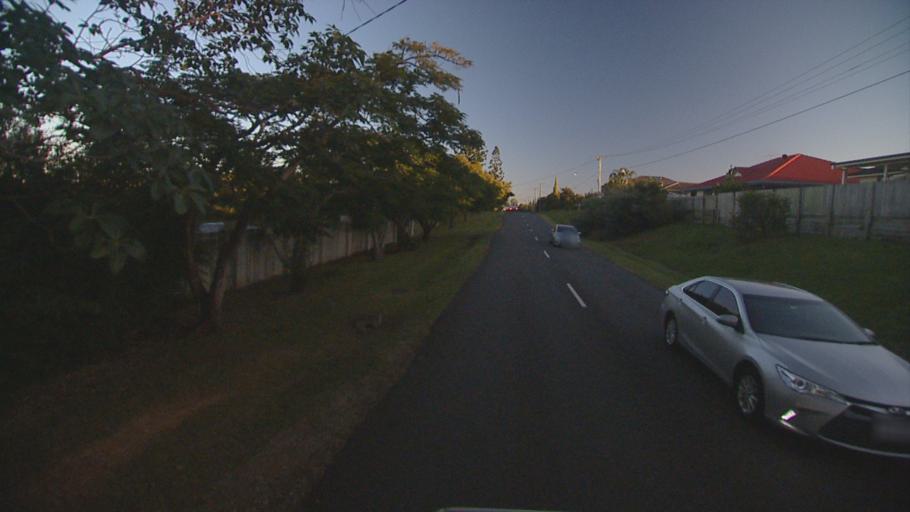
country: AU
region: Queensland
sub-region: Logan
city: Rochedale South
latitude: -27.6048
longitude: 153.1037
